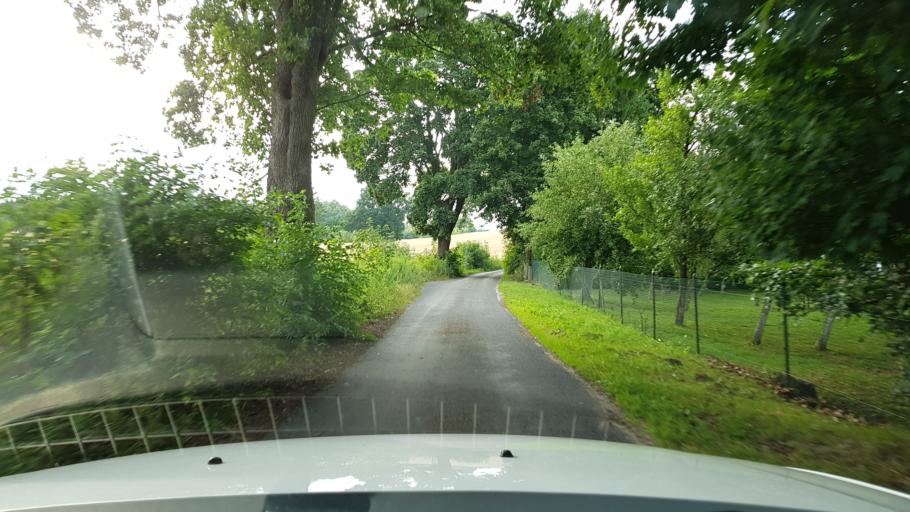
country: PL
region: West Pomeranian Voivodeship
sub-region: Powiat swidwinski
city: Polczyn-Zdroj
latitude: 53.7834
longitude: 16.0870
